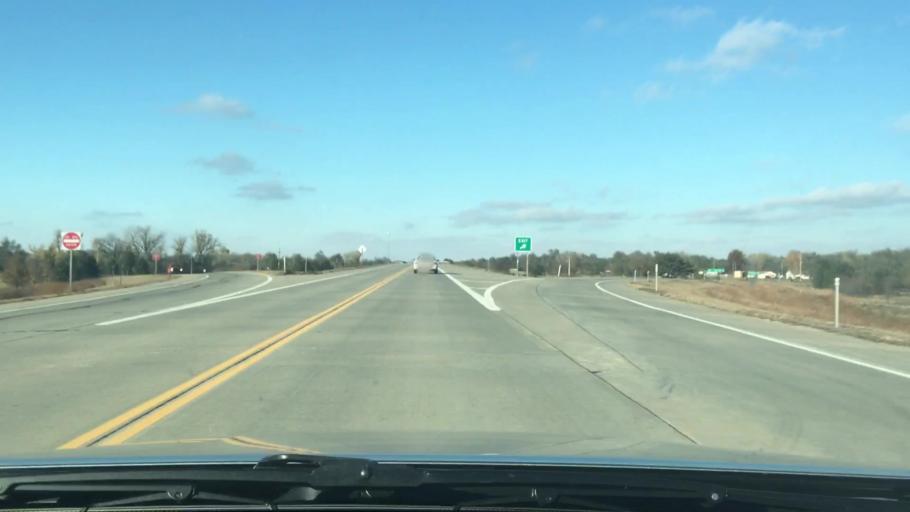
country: US
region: Kansas
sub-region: Reno County
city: South Hutchinson
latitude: 38.0544
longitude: -97.9859
